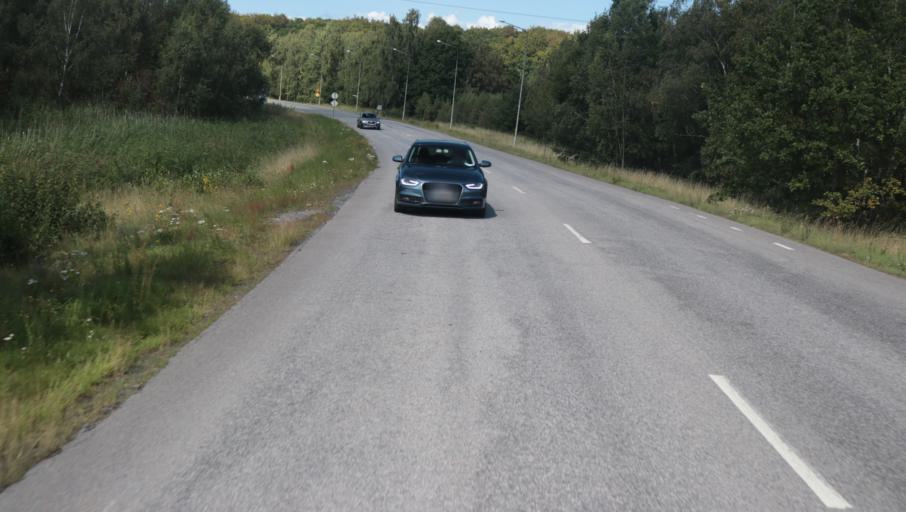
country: SE
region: Blekinge
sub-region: Karlshamns Kommun
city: Karlshamn
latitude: 56.1649
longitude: 14.8528
